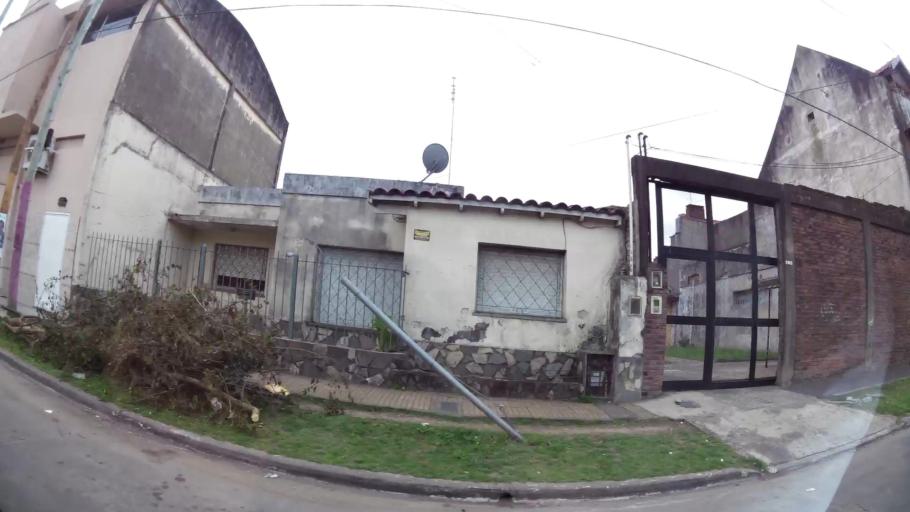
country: AR
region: Buenos Aires
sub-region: Partido de Quilmes
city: Quilmes
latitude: -34.7677
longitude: -58.2705
